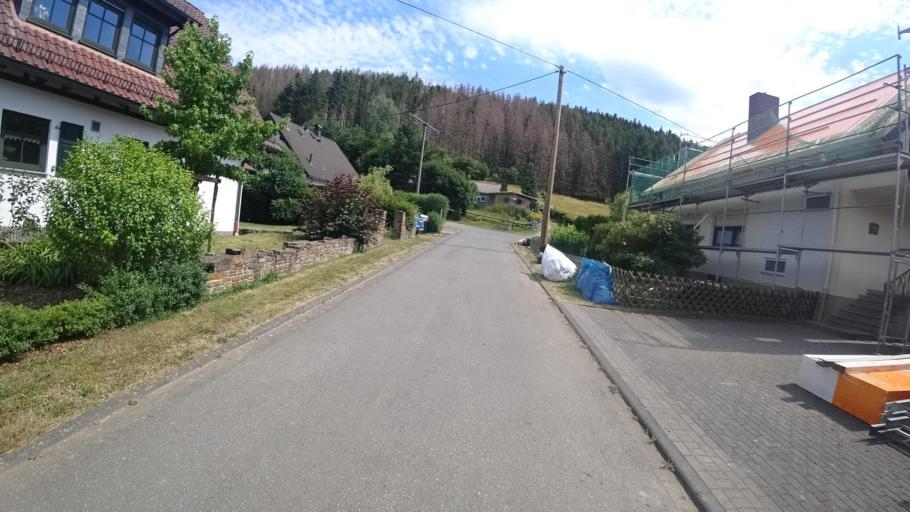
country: DE
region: Rheinland-Pfalz
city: Heckenbach
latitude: 50.4820
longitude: 7.0536
